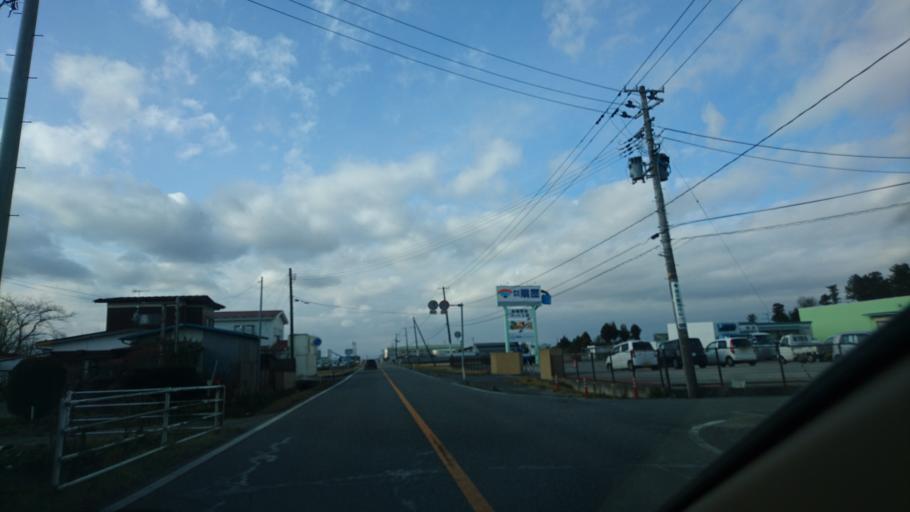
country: JP
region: Miyagi
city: Kogota
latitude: 38.5522
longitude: 141.0912
